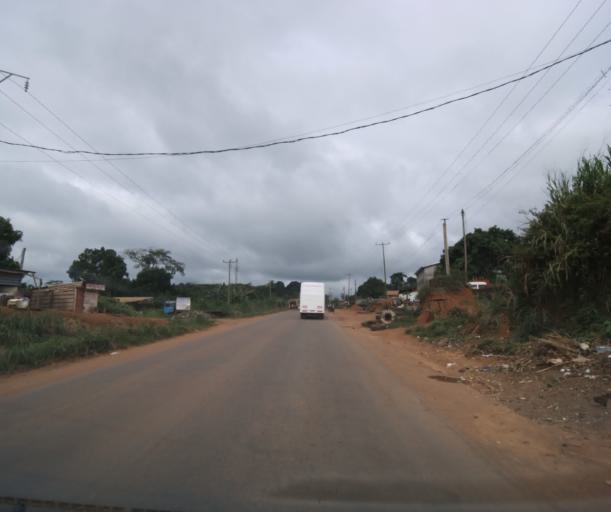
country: CM
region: Centre
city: Yaounde
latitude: 3.7971
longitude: 11.4995
